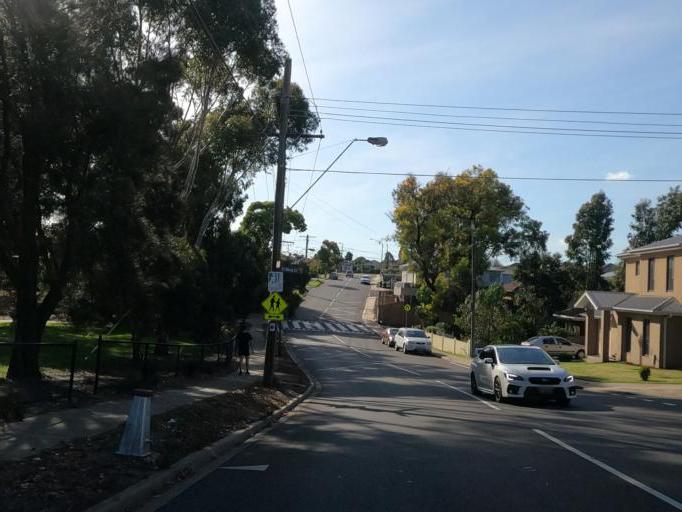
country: AU
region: Victoria
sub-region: Moonee Valley
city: Airport West
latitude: -37.7283
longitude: 144.8813
